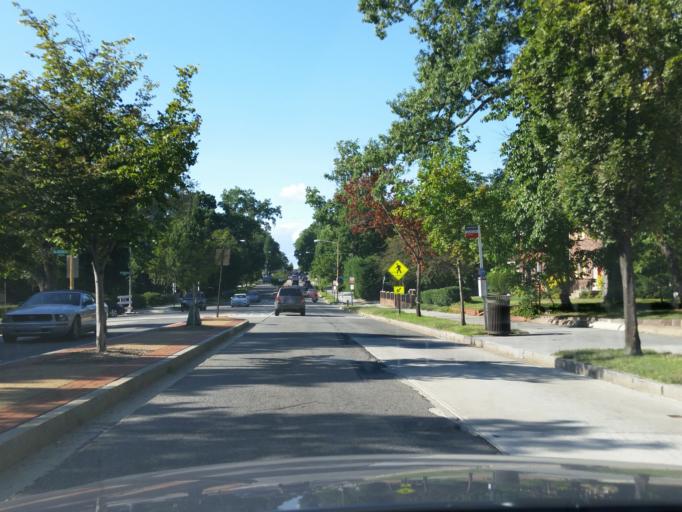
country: US
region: Maryland
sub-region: Montgomery County
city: Takoma Park
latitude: 38.9500
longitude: -77.0364
